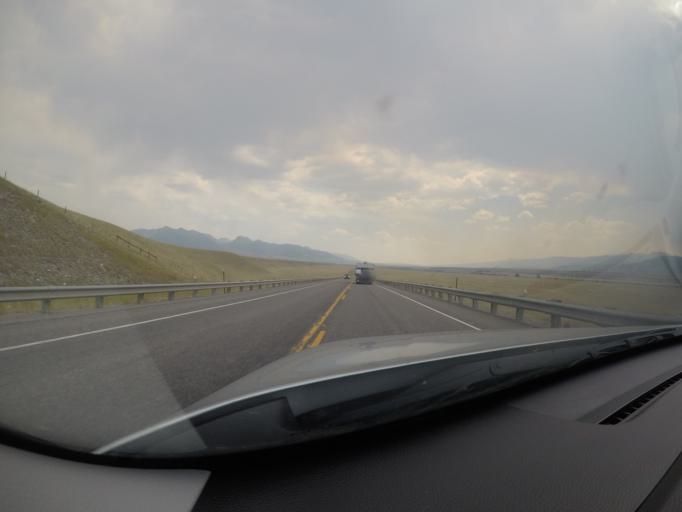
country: US
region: Montana
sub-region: Madison County
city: Virginia City
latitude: 45.1417
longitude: -111.6758
